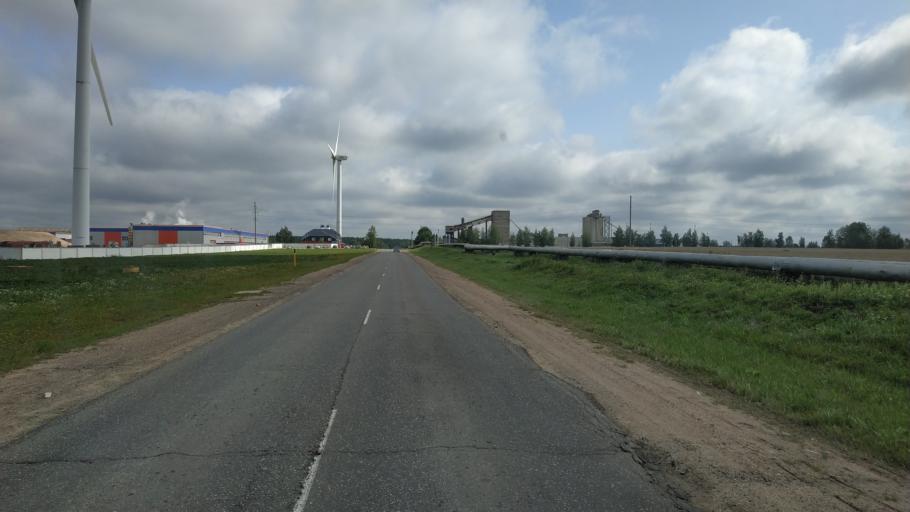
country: BY
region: Mogilev
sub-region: Mahilyowski Rayon
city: Veyno
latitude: 53.8385
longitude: 30.3739
